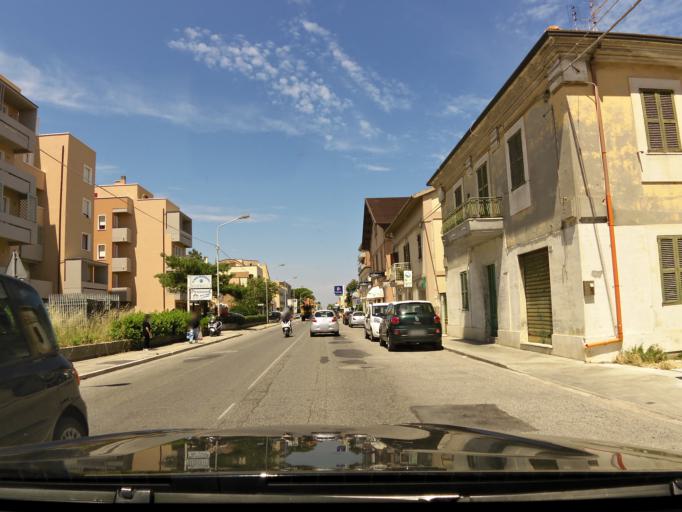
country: IT
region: The Marches
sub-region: Provincia di Ancona
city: Senigallia
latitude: 43.7209
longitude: 13.2132
